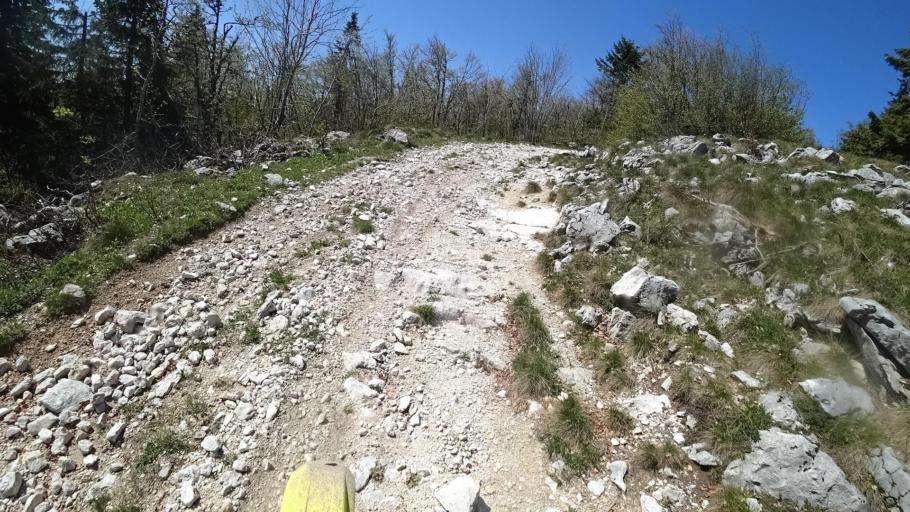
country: BA
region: Federation of Bosnia and Herzegovina
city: Rumboci
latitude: 43.8713
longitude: 17.4590
